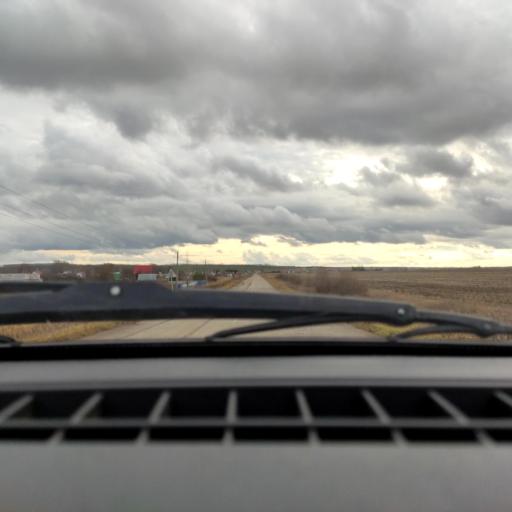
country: RU
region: Bashkortostan
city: Asanovo
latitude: 54.9376
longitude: 55.5172
